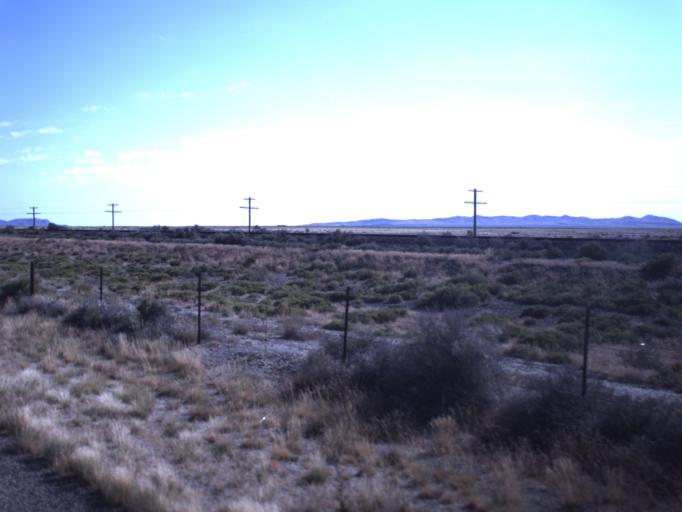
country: US
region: Utah
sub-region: Beaver County
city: Milford
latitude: 38.6468
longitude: -112.9827
